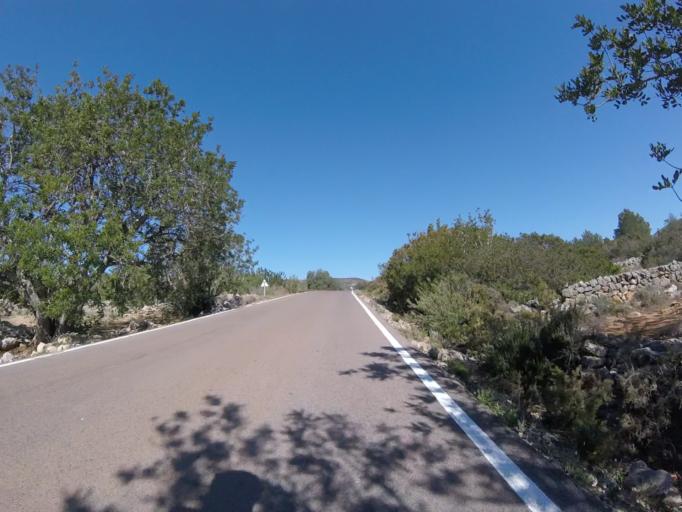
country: ES
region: Valencia
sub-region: Provincia de Castello
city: Santa Magdalena de Pulpis
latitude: 40.3745
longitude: 0.2719
